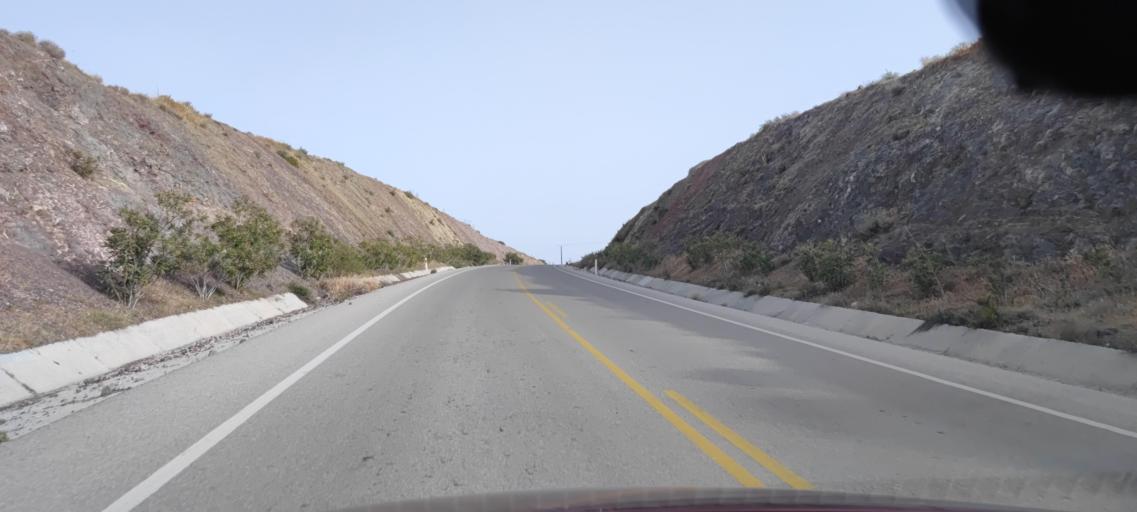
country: CY
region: Ammochostos
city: Leonarisso
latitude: 35.4865
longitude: 34.1022
